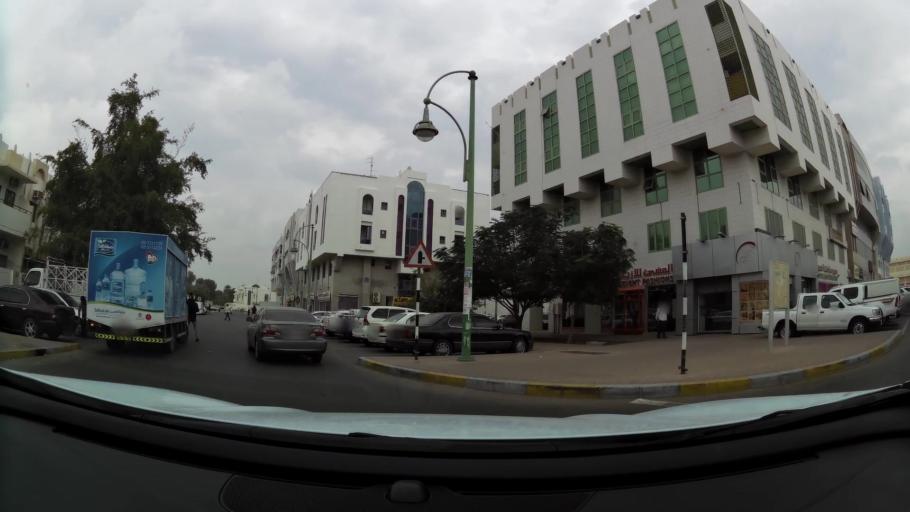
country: AE
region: Abu Dhabi
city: Al Ain
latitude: 24.2219
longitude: 55.7734
